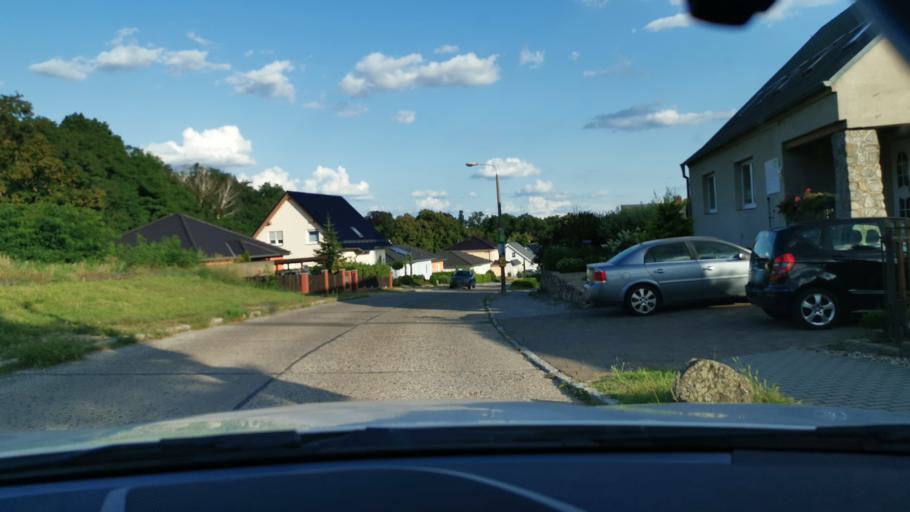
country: DE
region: Brandenburg
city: Juterbog
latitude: 52.0012
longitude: 13.0810
